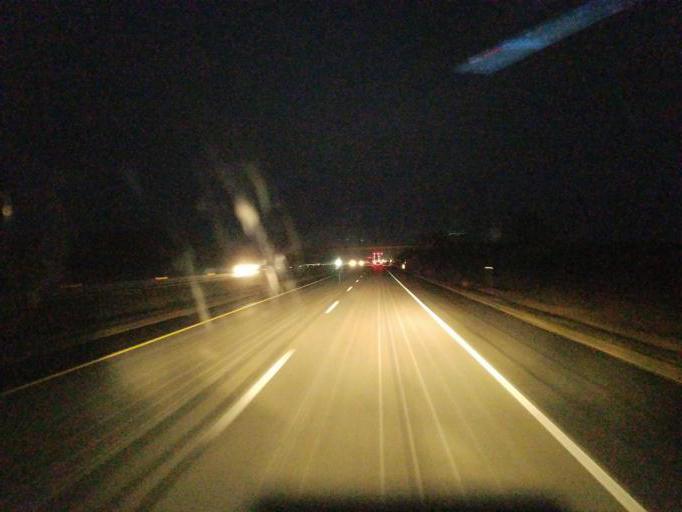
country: US
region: Iowa
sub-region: Guthrie County
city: Stuart
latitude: 41.4960
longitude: -94.3782
